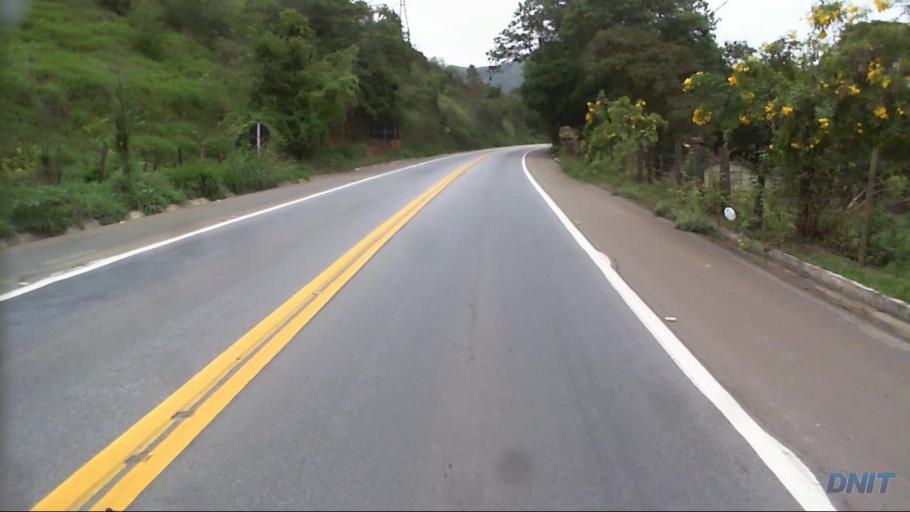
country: BR
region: Minas Gerais
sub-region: Timoteo
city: Timoteo
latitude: -19.5665
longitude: -42.7116
